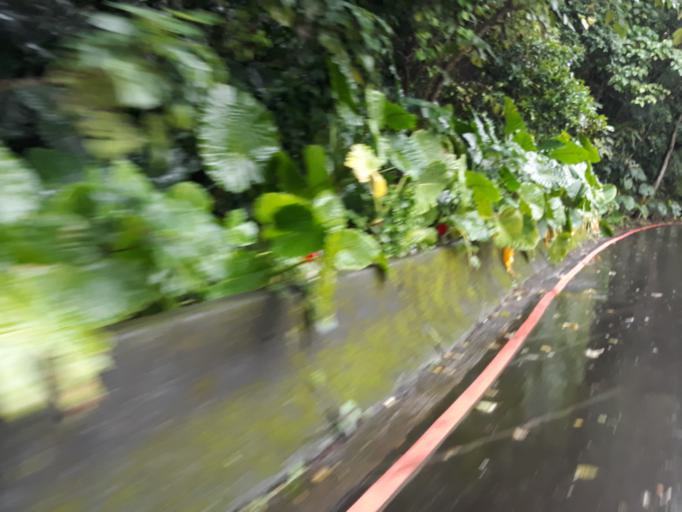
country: TW
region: Taipei
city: Taipei
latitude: 24.9934
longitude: 121.5907
